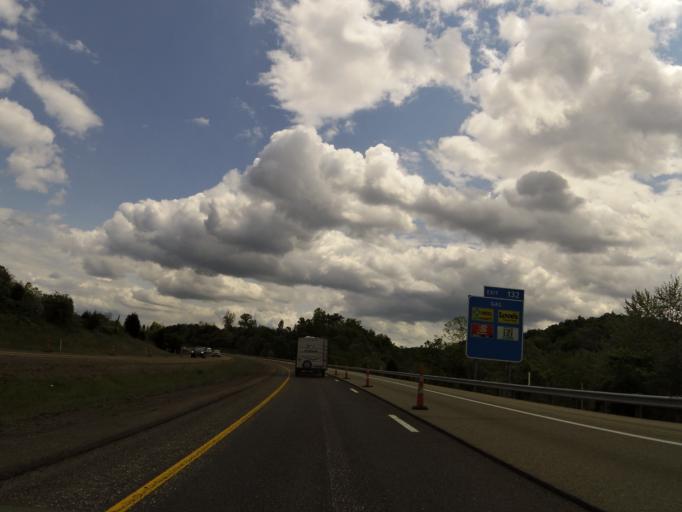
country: US
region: West Virginia
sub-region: Jackson County
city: Ripley
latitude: 38.7633
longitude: -81.7079
